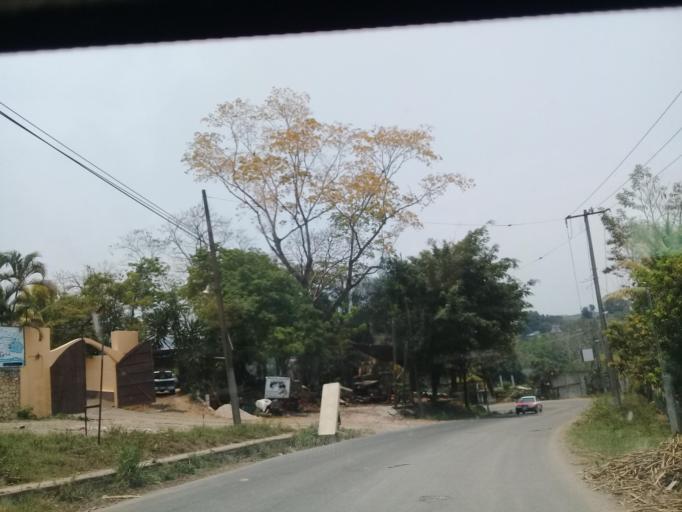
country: MX
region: Veracruz
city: Cosolapa
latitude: 18.5957
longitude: -96.6911
